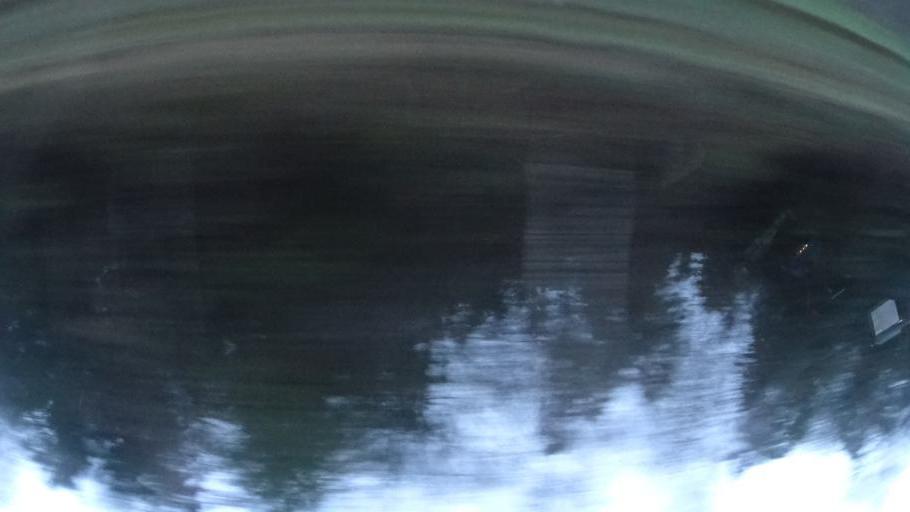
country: DE
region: Hesse
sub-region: Regierungsbezirk Kassel
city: Eichenzell
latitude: 50.4788
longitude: 9.6922
